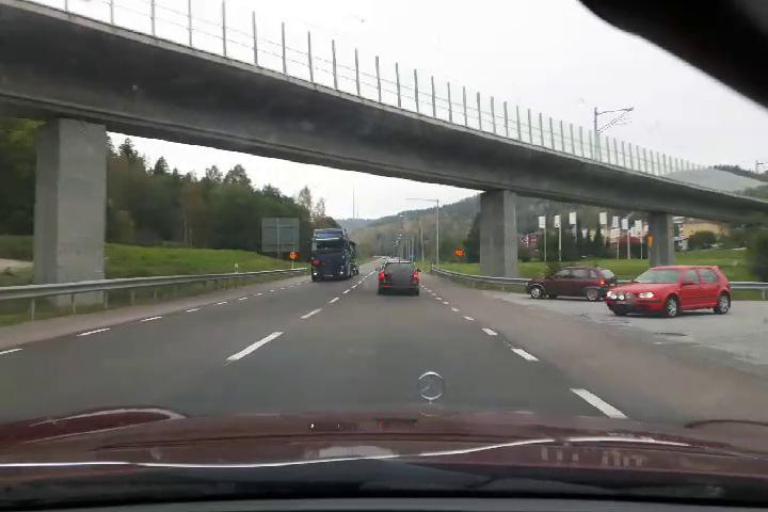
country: SE
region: Vaesternorrland
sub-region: OErnskoeldsviks Kommun
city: Ornskoldsvik
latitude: 63.2934
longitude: 18.6976
